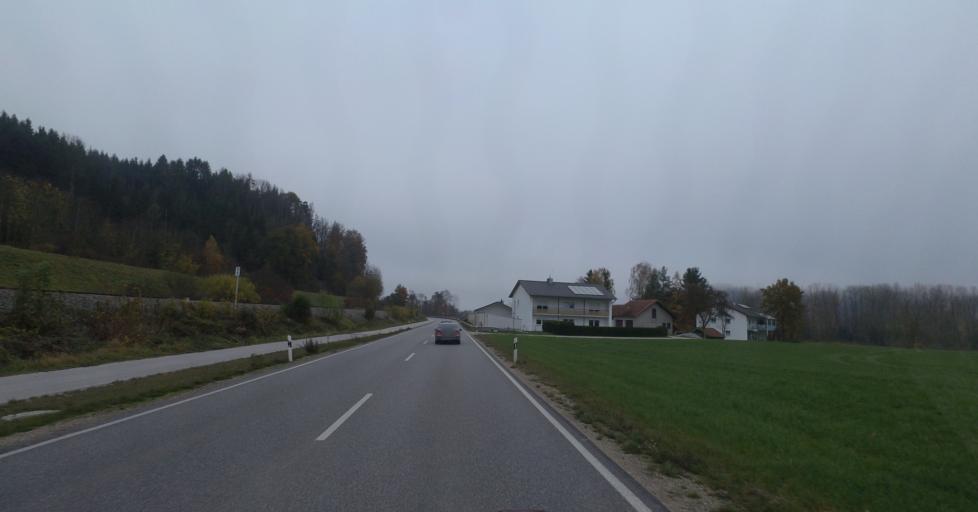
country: DE
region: Bavaria
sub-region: Upper Bavaria
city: Engelsberg
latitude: 48.1118
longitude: 12.5695
